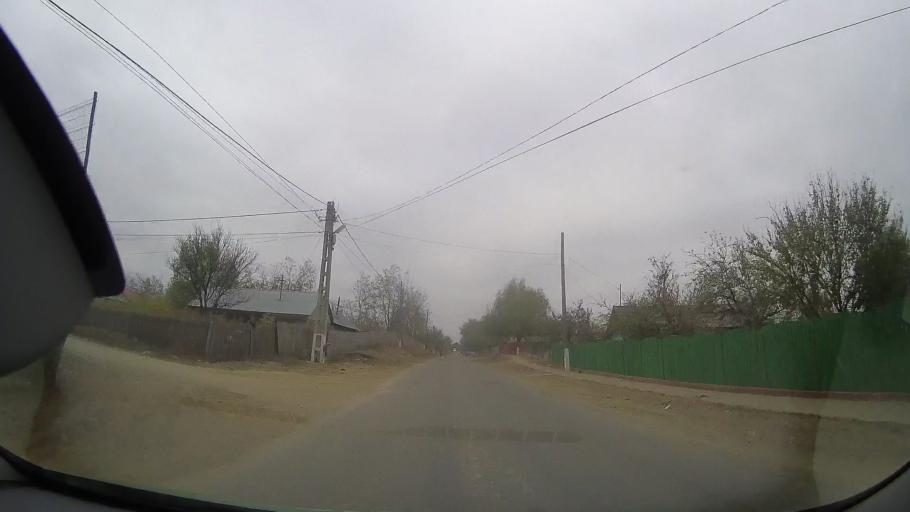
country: RO
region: Buzau
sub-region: Comuna Luciu
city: Luciu
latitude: 44.9683
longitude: 27.0920
